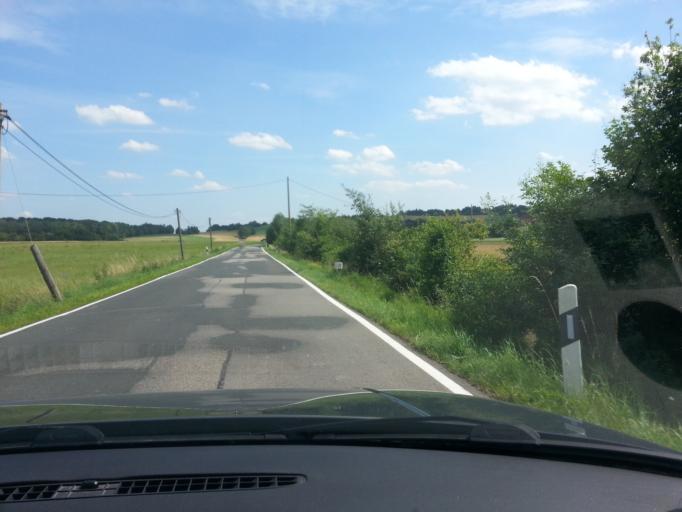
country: DE
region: Saarland
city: Blieskastel
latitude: 49.2017
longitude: 7.2811
